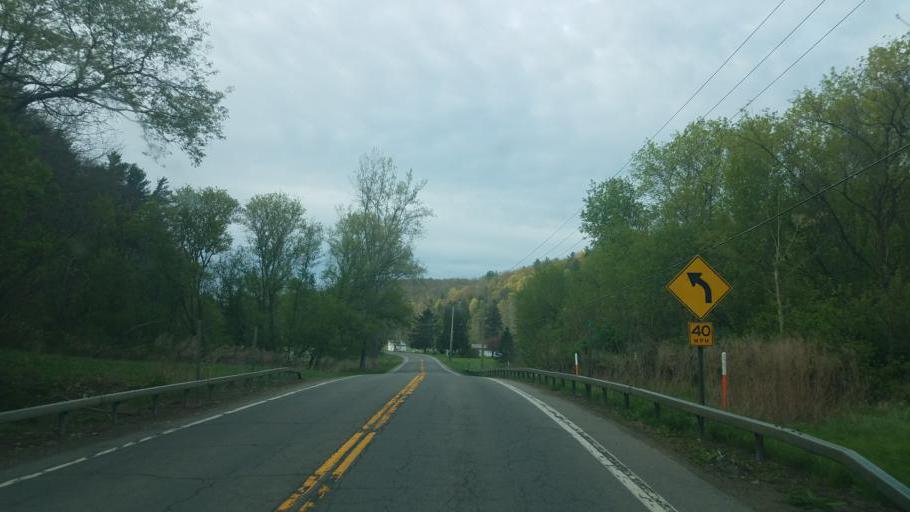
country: US
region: New York
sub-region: Steuben County
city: Canisteo
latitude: 42.2466
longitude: -77.5833
